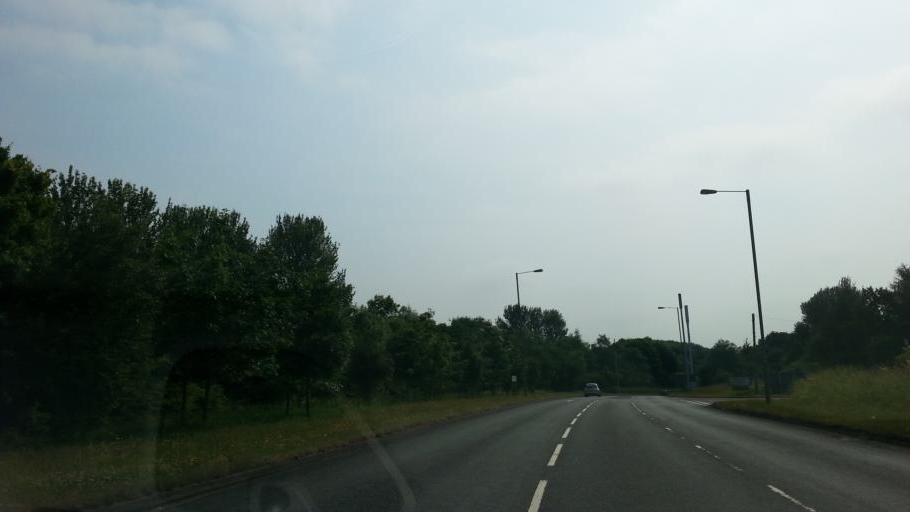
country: GB
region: England
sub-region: Warwickshire
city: Studley
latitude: 52.2998
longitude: -1.8946
